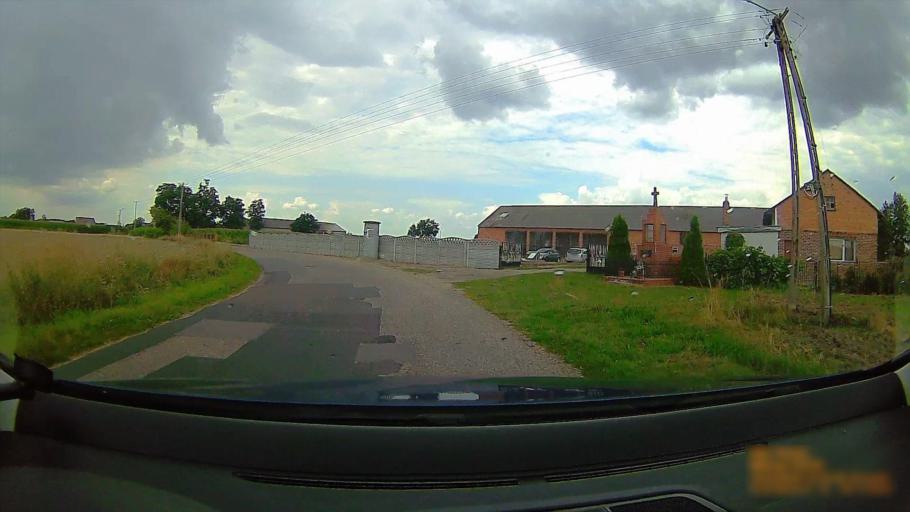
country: PL
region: Greater Poland Voivodeship
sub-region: Powiat koninski
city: Rychwal
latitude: 52.1069
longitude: 18.1883
